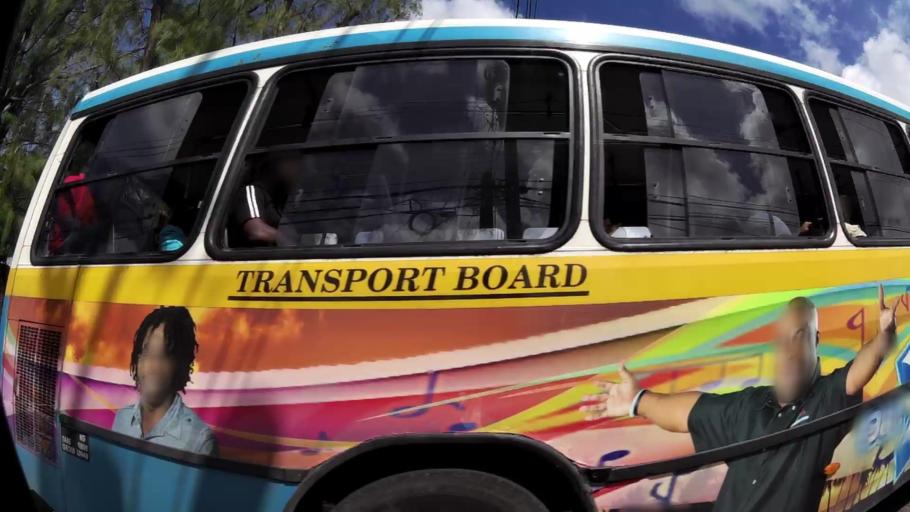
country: BB
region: Saint Michael
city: Bridgetown
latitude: 13.1282
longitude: -59.6289
